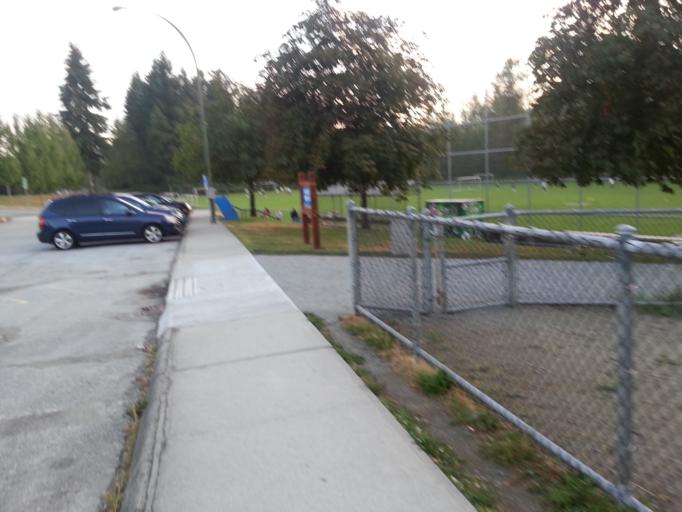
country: CA
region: British Columbia
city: Port Moody
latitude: 49.2837
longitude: -122.8794
